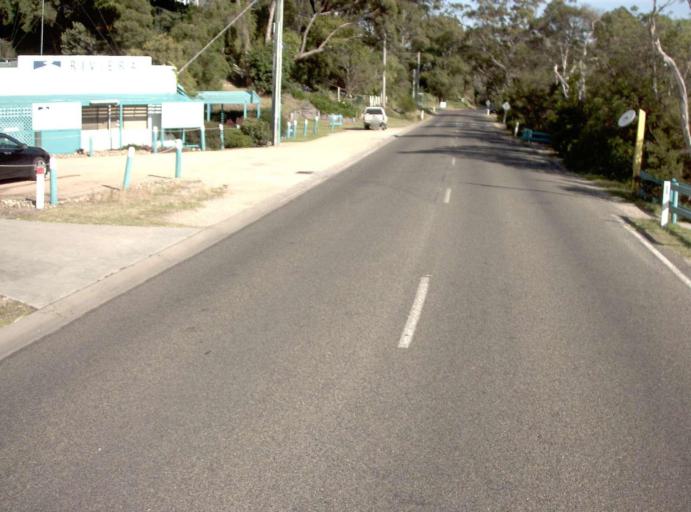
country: AU
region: Victoria
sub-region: East Gippsland
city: Lakes Entrance
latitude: -37.8813
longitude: 147.8599
